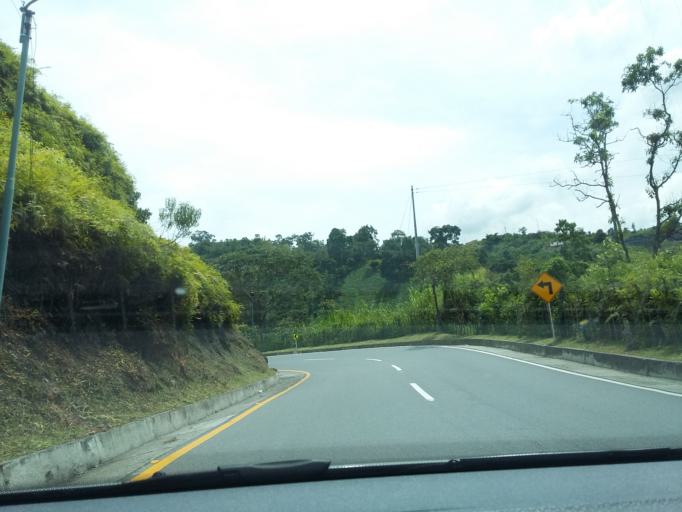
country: CO
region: Santander
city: Bucaramanga
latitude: 7.1132
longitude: -73.0788
